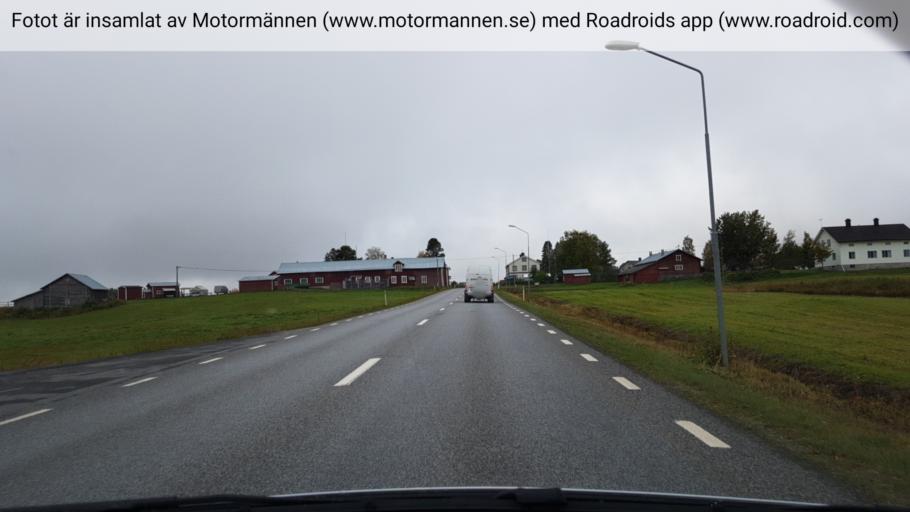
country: SE
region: Jaemtland
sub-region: Stroemsunds Kommun
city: Stroemsund
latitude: 63.4992
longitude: 15.2587
